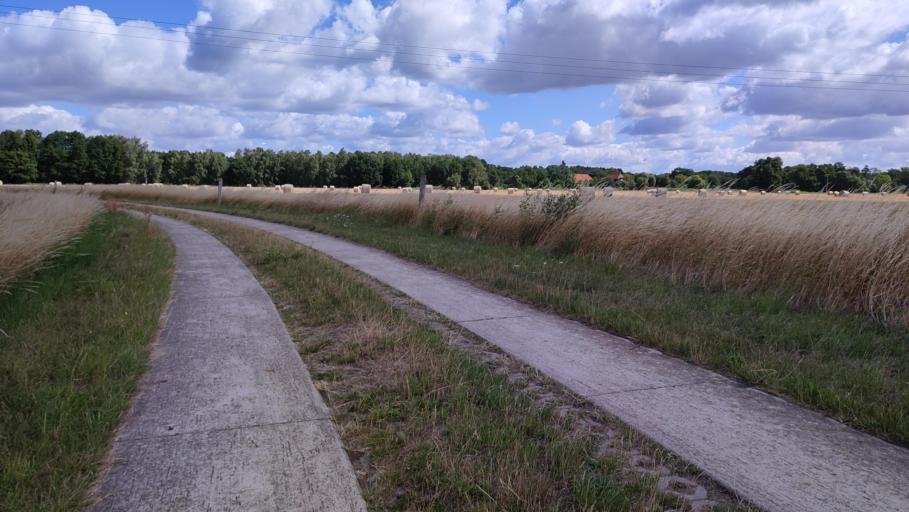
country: DE
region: Lower Saxony
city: Neu Darchau
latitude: 53.2307
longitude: 10.9705
